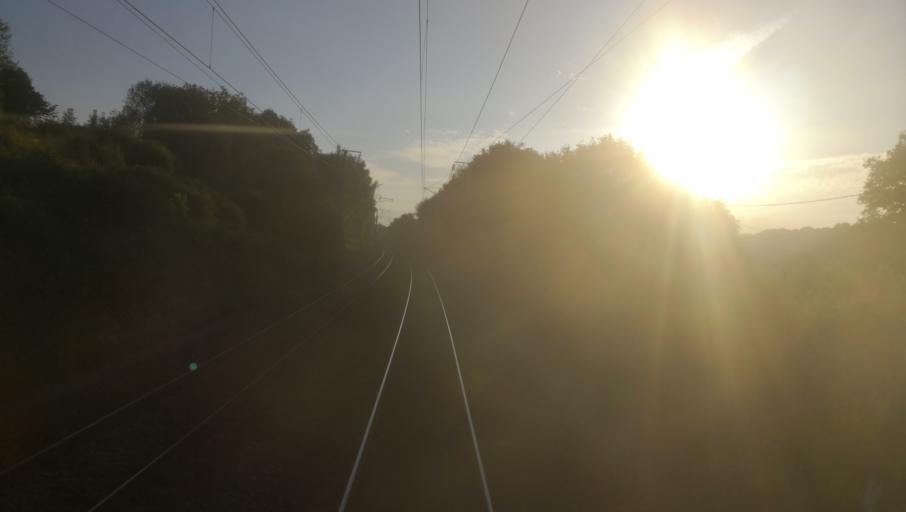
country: FR
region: Lower Normandy
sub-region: Departement du Calvados
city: Beuvillers
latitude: 49.1221
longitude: 0.3265
